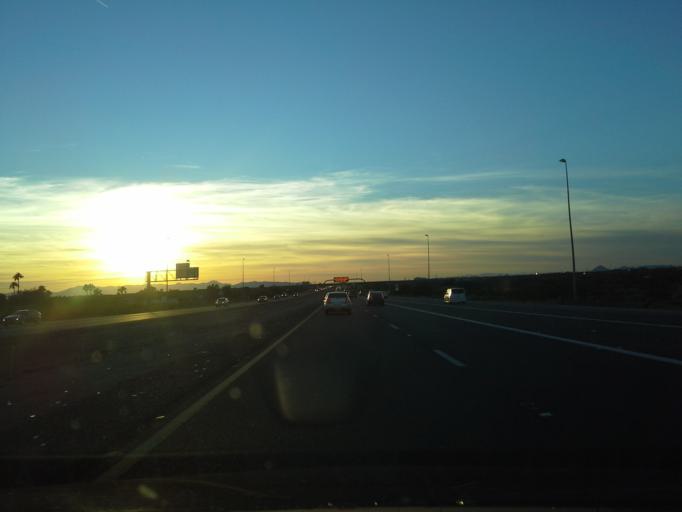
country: US
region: Arizona
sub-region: Pinal County
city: Apache Junction
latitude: 33.3867
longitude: -111.5679
